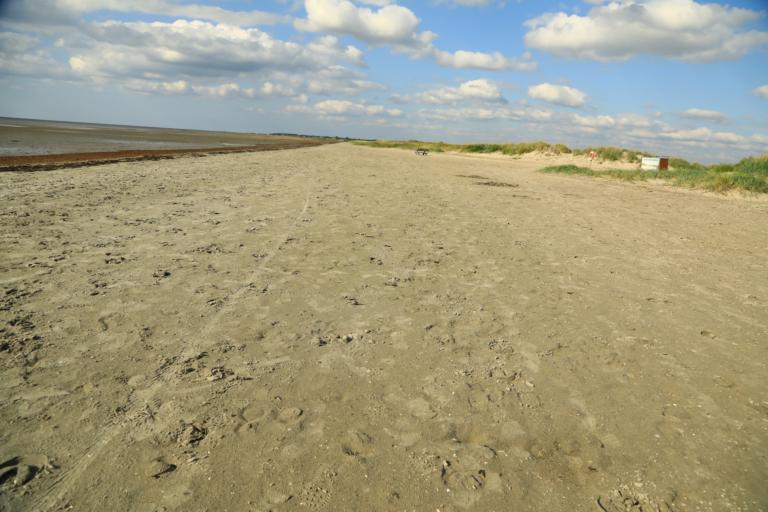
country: SE
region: Halland
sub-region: Varbergs Kommun
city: Tvaaker
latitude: 57.0072
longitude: 12.3483
